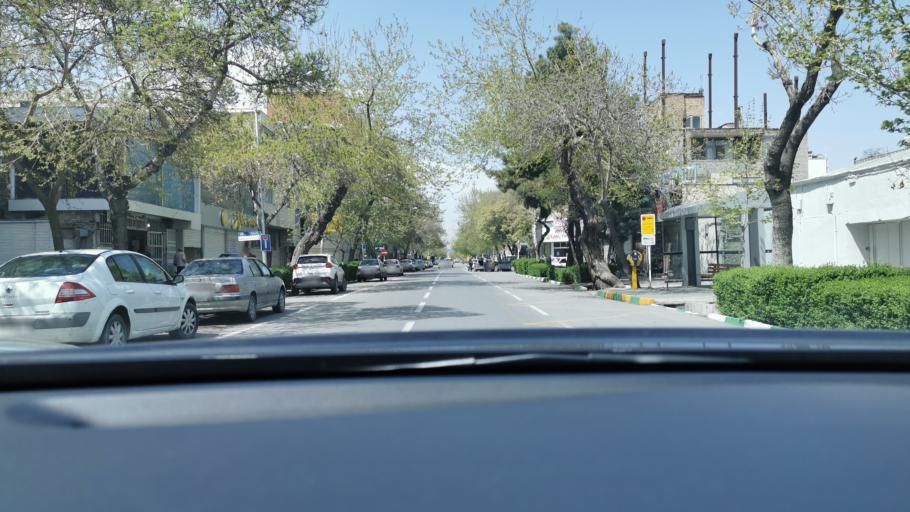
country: IR
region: Razavi Khorasan
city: Mashhad
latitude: 36.2979
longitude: 59.5932
